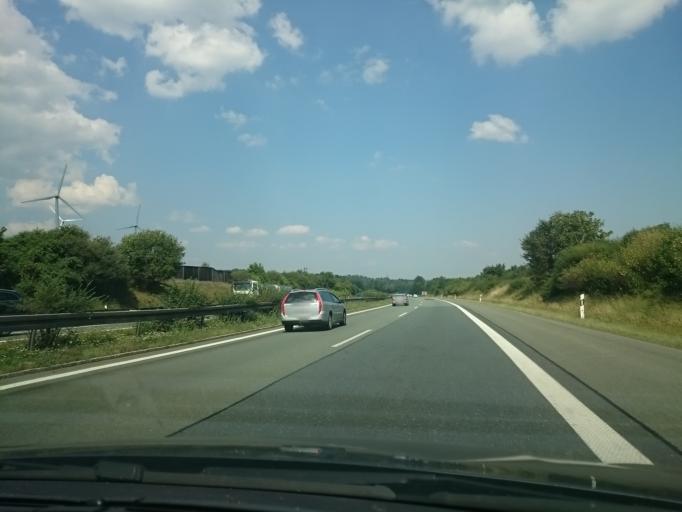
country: DE
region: Saxony
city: Treuen
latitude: 50.5629
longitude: 12.2844
